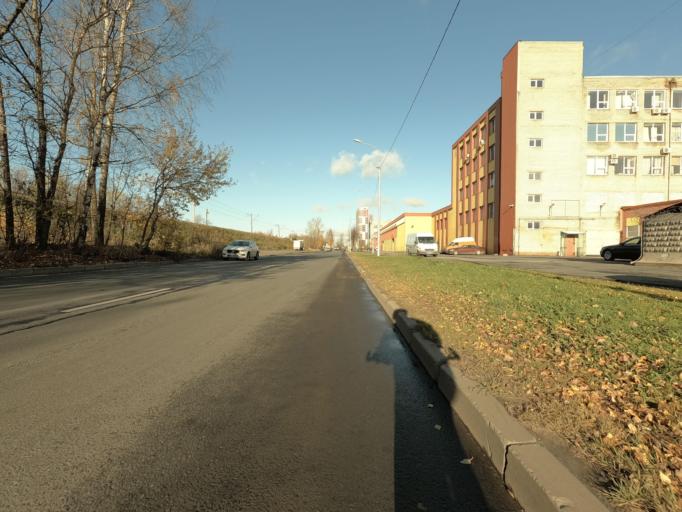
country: RU
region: St.-Petersburg
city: Krasnogvargeisky
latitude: 59.9508
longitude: 30.4478
